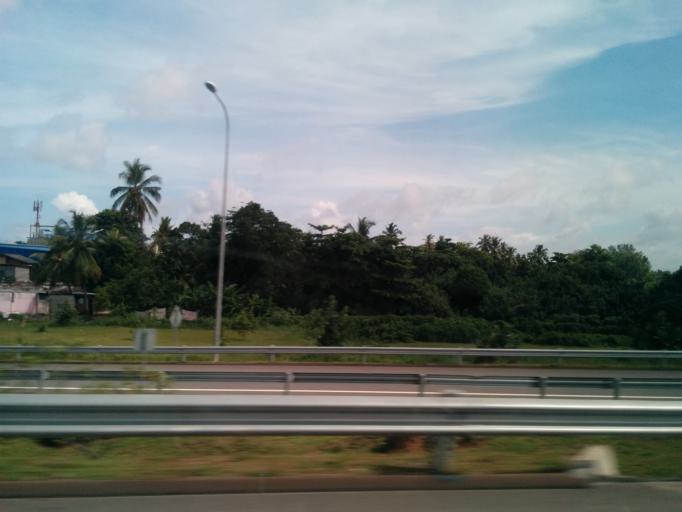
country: LK
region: Western
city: Peliyagoda
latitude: 6.9569
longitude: 79.8839
